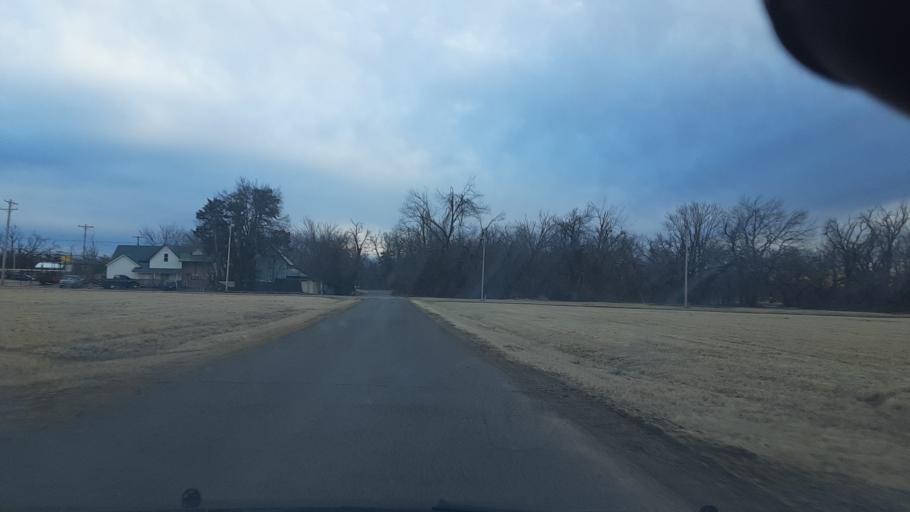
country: US
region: Oklahoma
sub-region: Logan County
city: Guthrie
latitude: 35.8727
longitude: -97.4266
